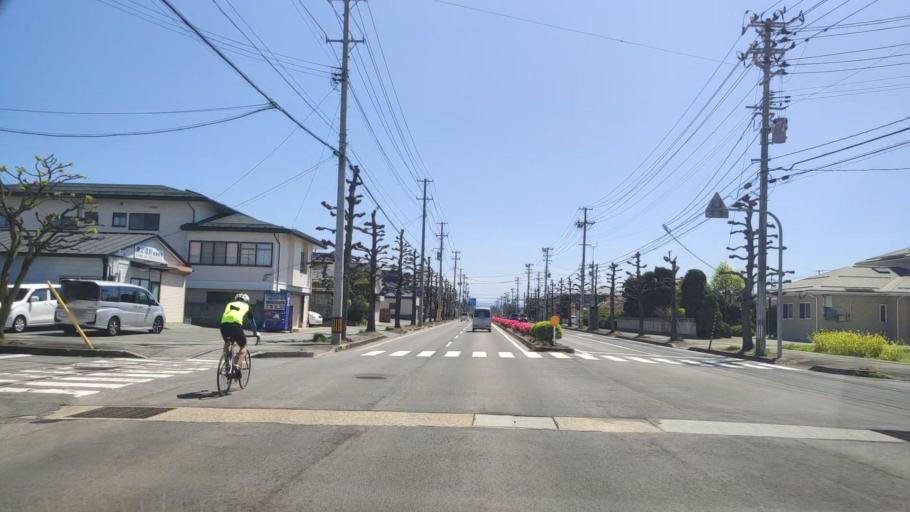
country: JP
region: Yamagata
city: Tendo
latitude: 38.3694
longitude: 140.3679
